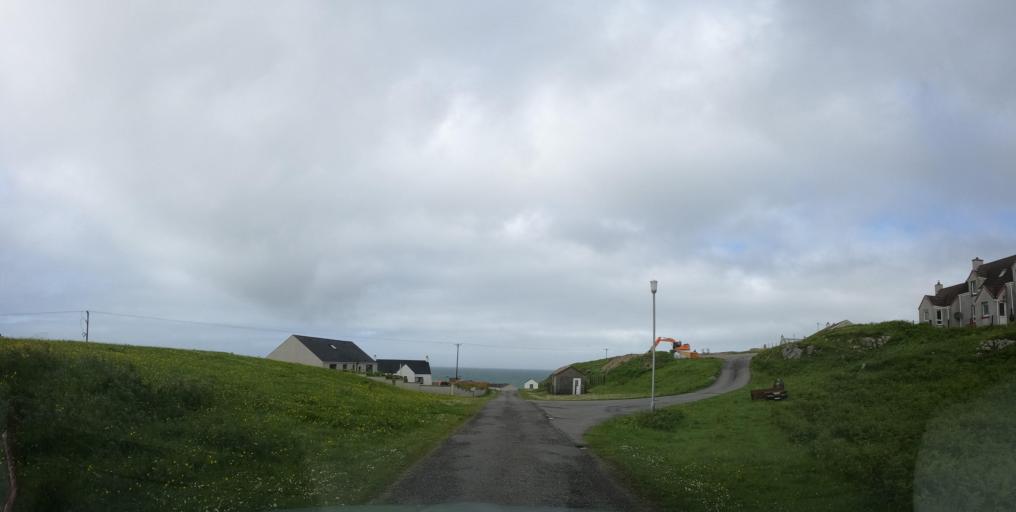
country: GB
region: Scotland
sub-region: Eilean Siar
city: Isle of South Uist
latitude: 57.0855
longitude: -7.3065
